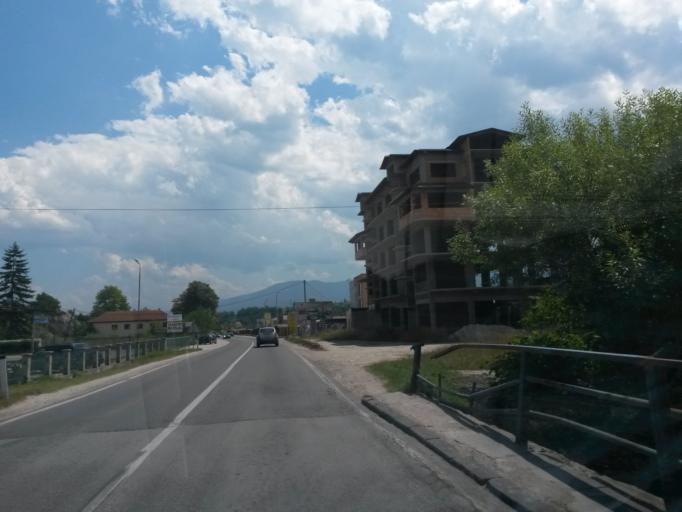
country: BA
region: Federation of Bosnia and Herzegovina
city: Vitez
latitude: 44.1742
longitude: 17.7572
